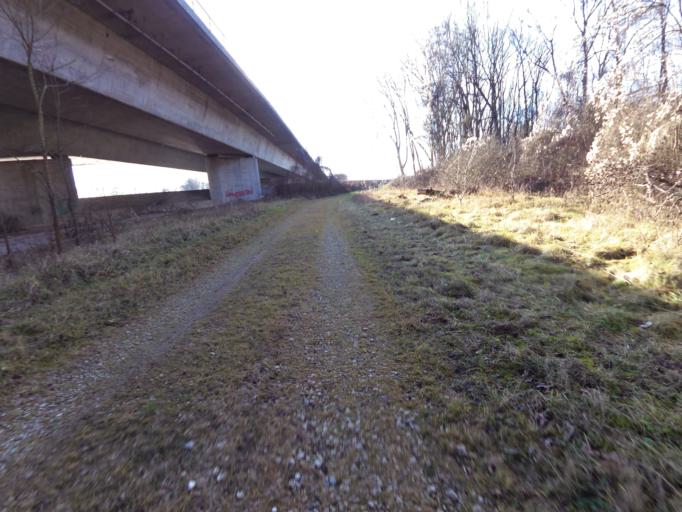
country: DE
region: Bavaria
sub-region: Lower Bavaria
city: Bruckberg
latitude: 48.4958
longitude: 12.0041
